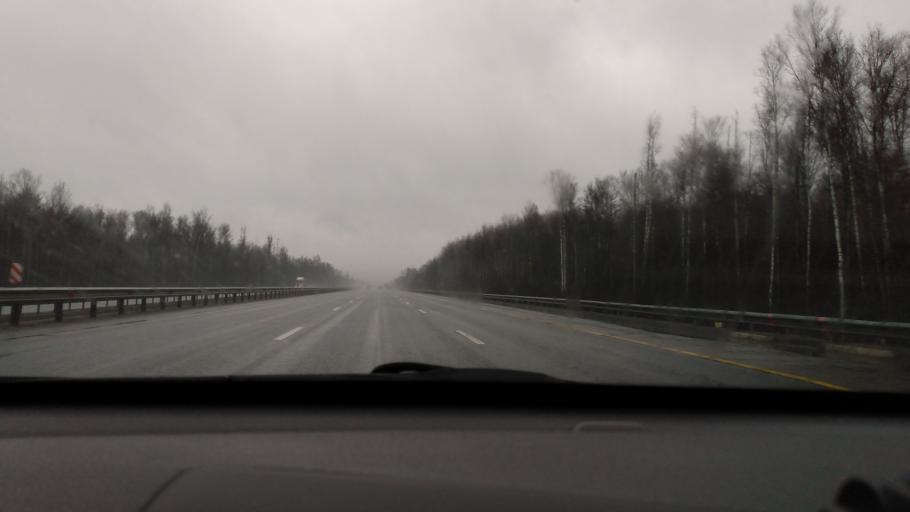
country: RU
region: Moskovskaya
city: Zhilevo
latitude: 54.9385
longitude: 37.9898
